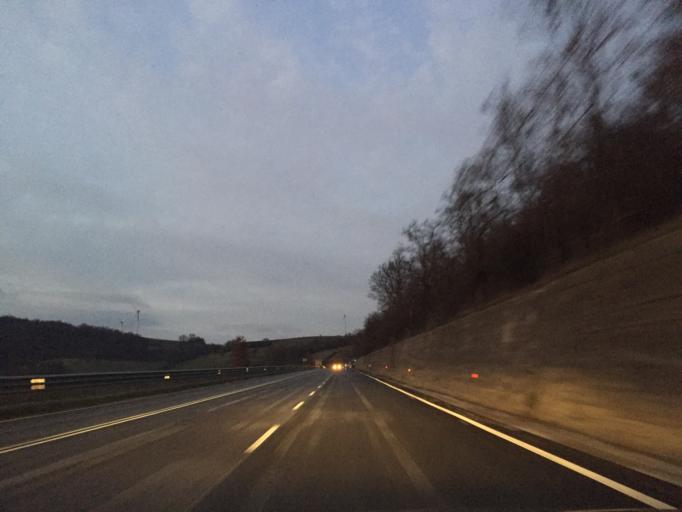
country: IT
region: Apulia
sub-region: Provincia di Foggia
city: Volturino
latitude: 41.4638
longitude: 15.0935
